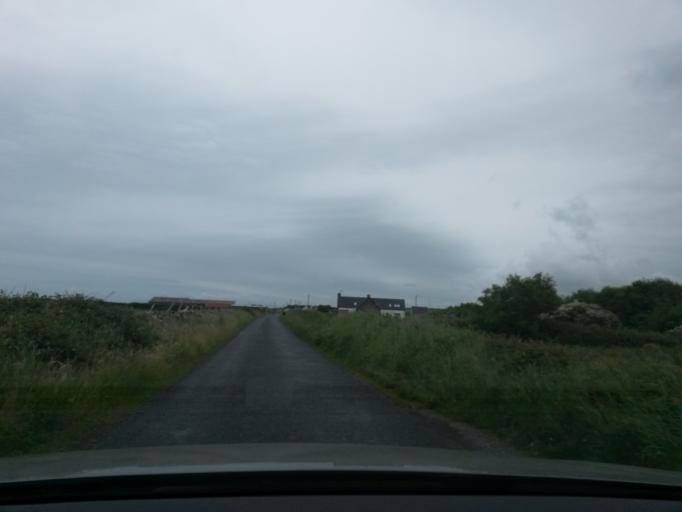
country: IE
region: Connaught
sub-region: Sligo
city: Tobercurry
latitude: 54.2527
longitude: -8.8198
